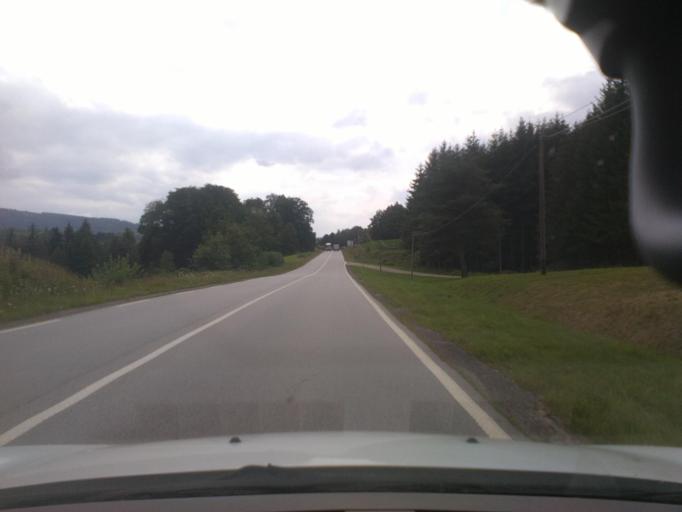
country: FR
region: Lorraine
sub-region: Departement des Vosges
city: Docelles
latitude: 48.1546
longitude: 6.6268
